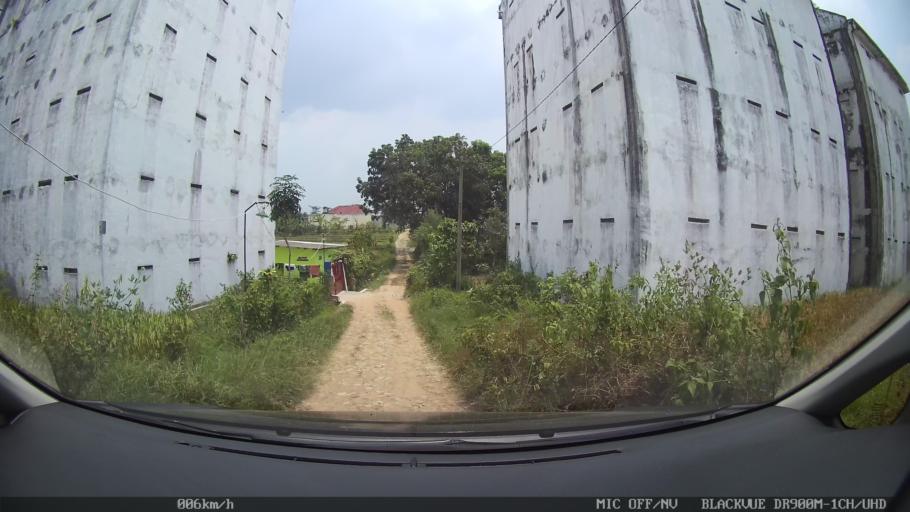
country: ID
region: Lampung
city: Pringsewu
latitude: -5.3514
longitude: 104.9623
